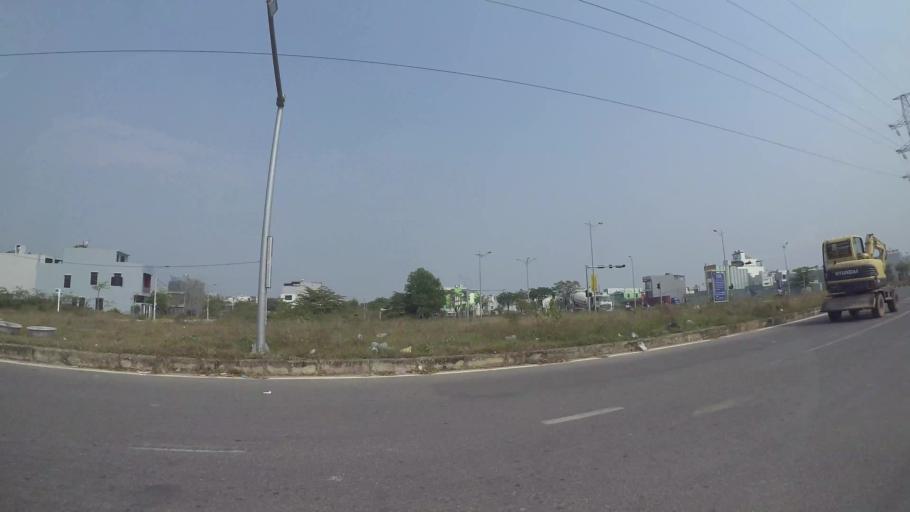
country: VN
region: Da Nang
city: Cam Le
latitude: 16.0075
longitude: 108.2194
